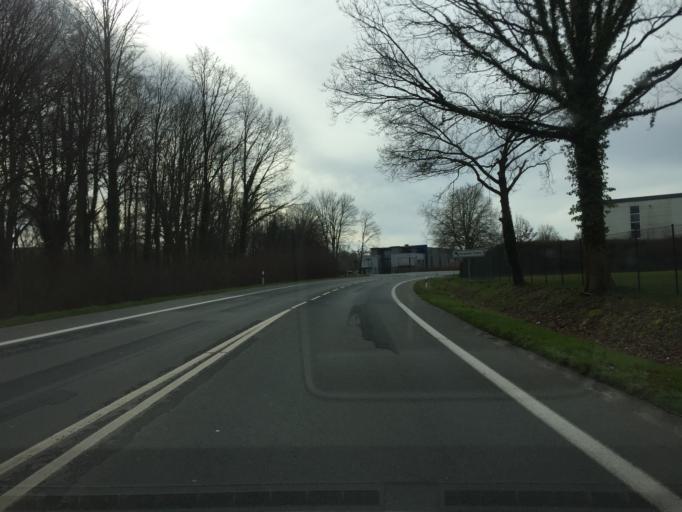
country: DE
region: North Rhine-Westphalia
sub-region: Regierungsbezirk Detmold
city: Vlotho
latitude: 52.1366
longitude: 8.8323
